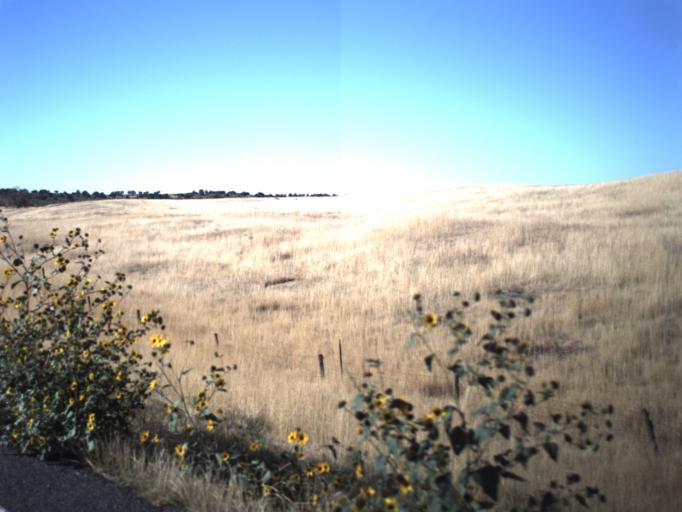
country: US
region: Utah
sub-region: Millard County
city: Delta
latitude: 39.5243
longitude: -112.2734
